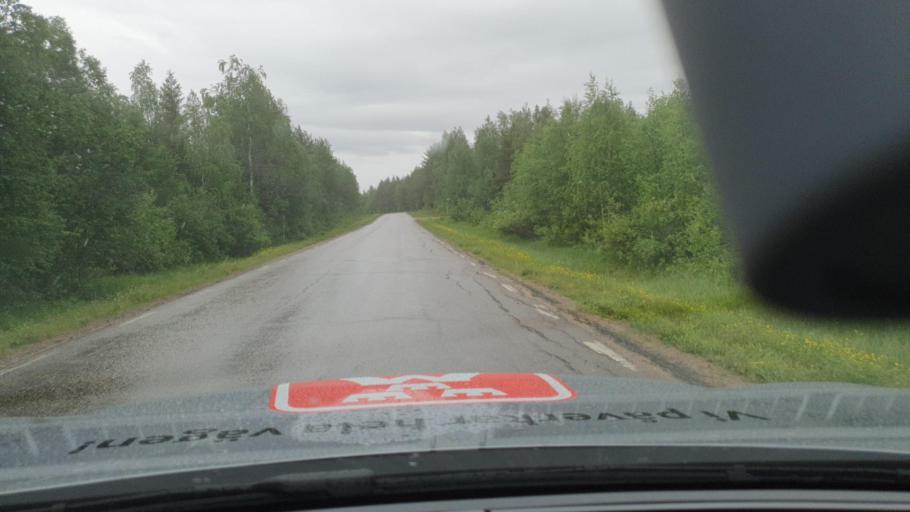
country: SE
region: Norrbotten
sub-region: Pajala Kommun
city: Pajala
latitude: 66.8444
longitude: 23.0713
